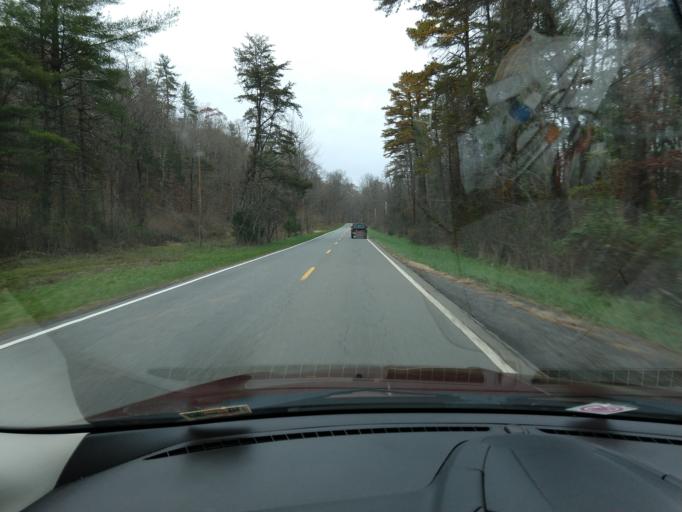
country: US
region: Virginia
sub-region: City of Covington
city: Covington
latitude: 37.7773
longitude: -80.1083
